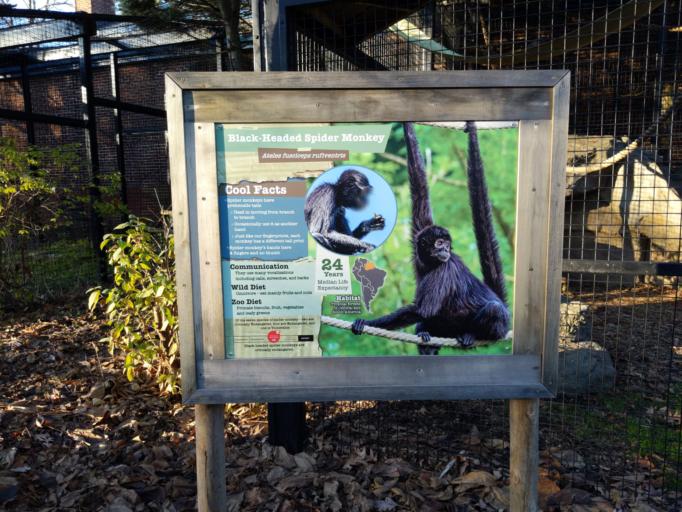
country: US
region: Michigan
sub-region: Ingham County
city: Lansing
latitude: 42.7181
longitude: -84.5249
